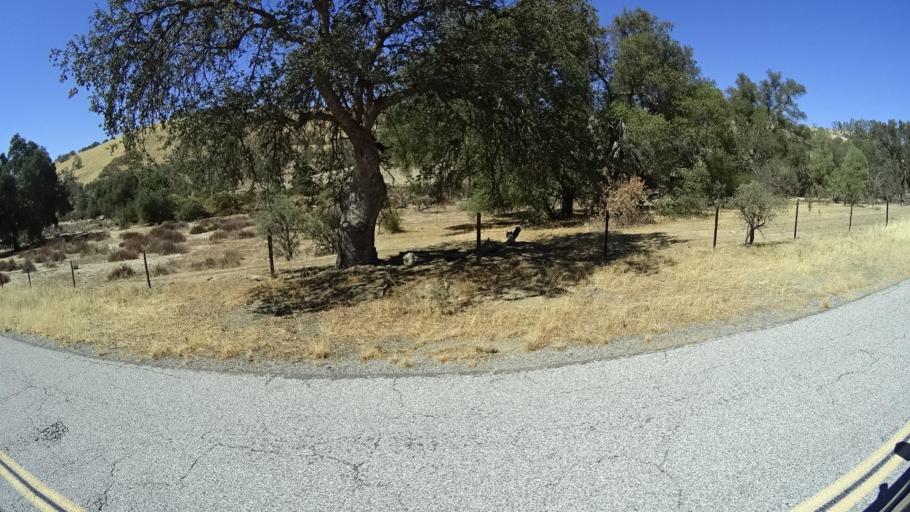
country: US
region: California
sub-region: San Luis Obispo County
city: San Miguel
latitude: 35.8753
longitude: -120.5669
